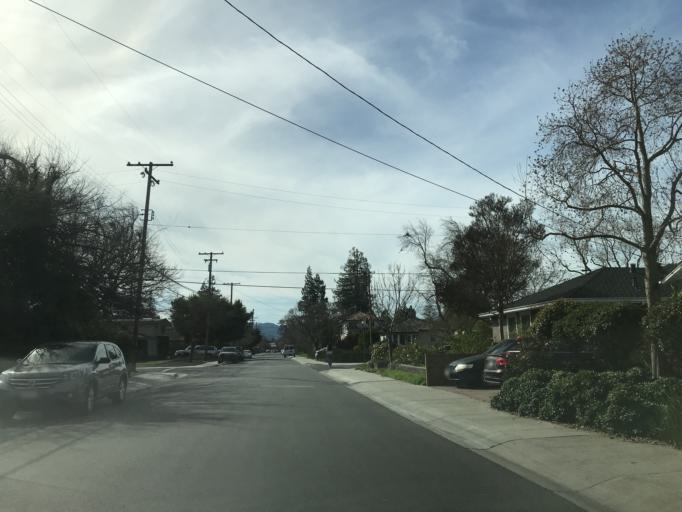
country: US
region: California
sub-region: Santa Clara County
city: Palo Alto
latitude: 37.4301
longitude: -122.1308
